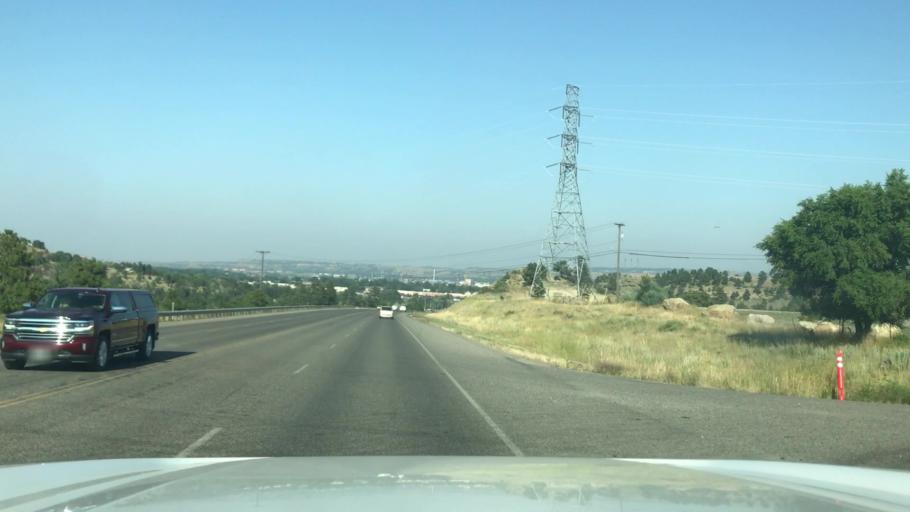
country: US
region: Montana
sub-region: Yellowstone County
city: Billings
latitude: 45.7998
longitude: -108.4975
